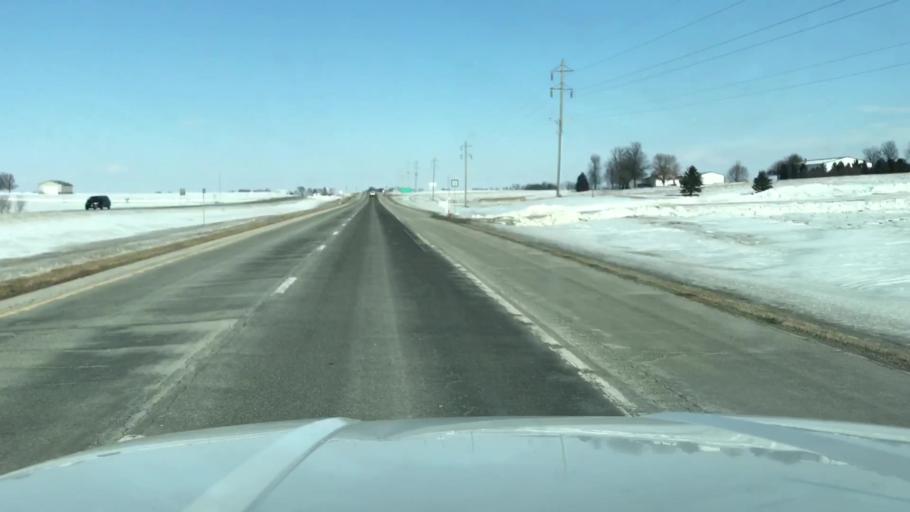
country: US
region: Missouri
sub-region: Nodaway County
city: Maryville
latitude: 40.2553
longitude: -94.8669
